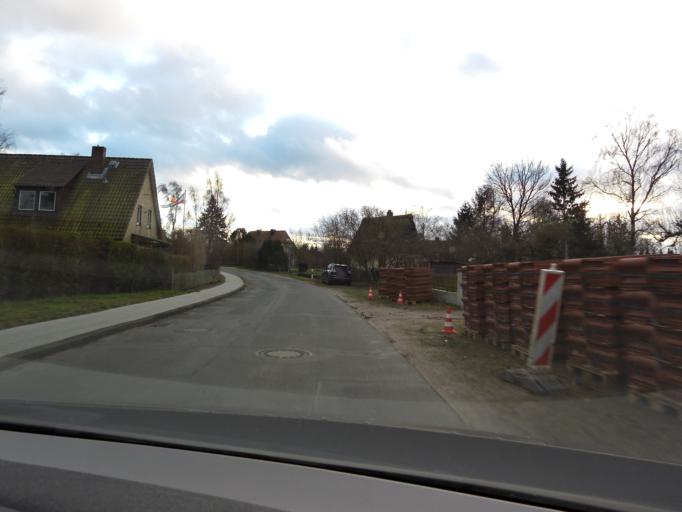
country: DE
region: Schleswig-Holstein
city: Seedorf
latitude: 53.6241
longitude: 10.8594
